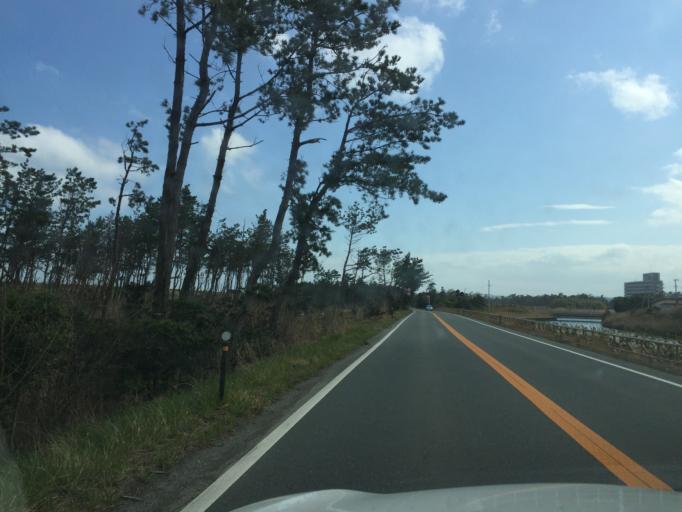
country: JP
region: Fukushima
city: Iwaki
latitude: 37.0500
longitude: 140.9722
